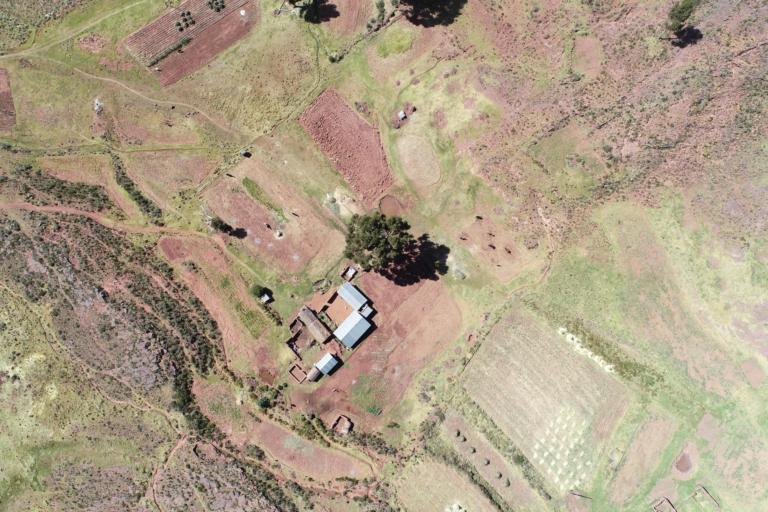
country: BO
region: La Paz
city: Tiahuanaco
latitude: -16.6043
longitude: -68.7794
